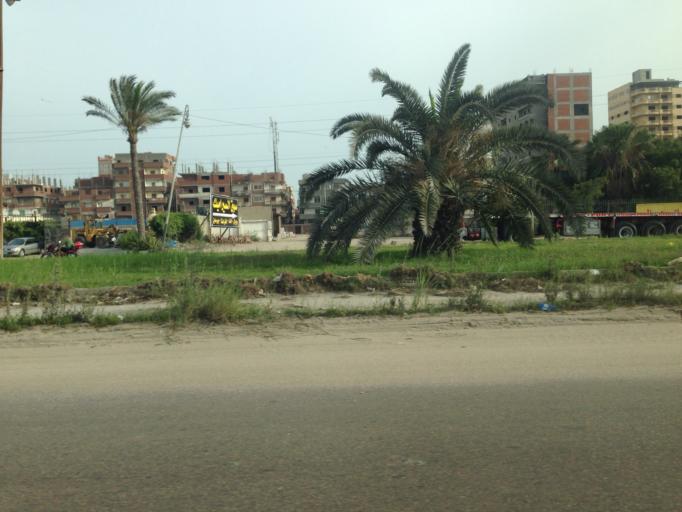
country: EG
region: Alexandria
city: Alexandria
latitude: 31.2039
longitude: 29.9880
